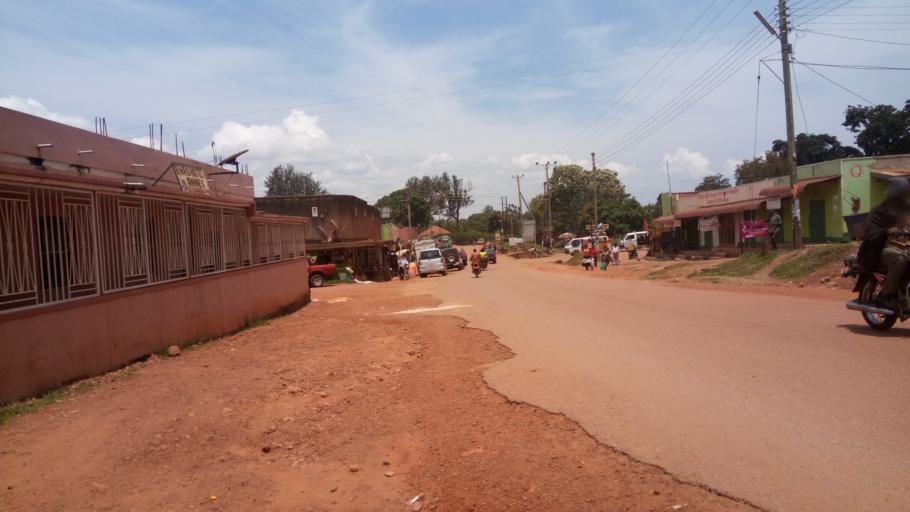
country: UG
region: Central Region
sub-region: Mityana District
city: Mityana
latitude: 0.3989
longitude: 32.0432
